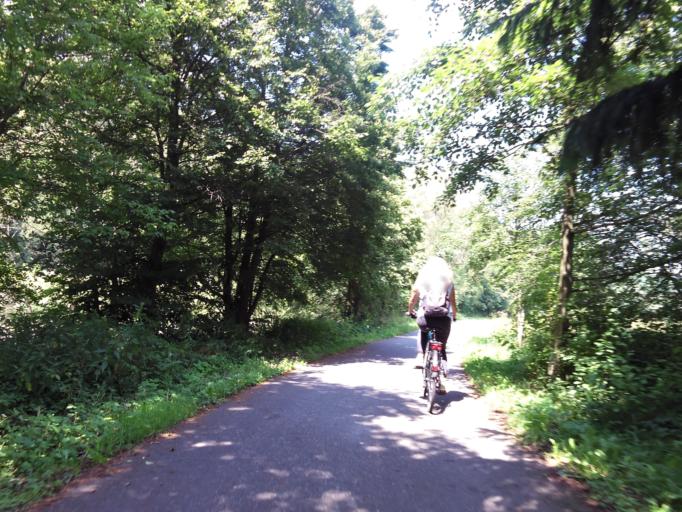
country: PL
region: Silesian Voivodeship
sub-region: Powiat zywiecki
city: Rajcza
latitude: 49.5276
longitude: 19.1065
